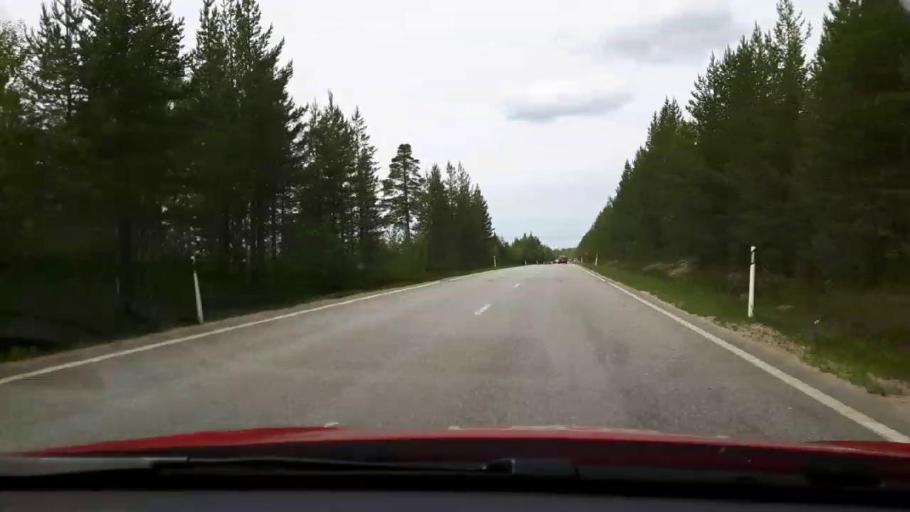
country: SE
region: Jaemtland
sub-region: Harjedalens Kommun
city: Sveg
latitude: 62.0525
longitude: 14.3090
